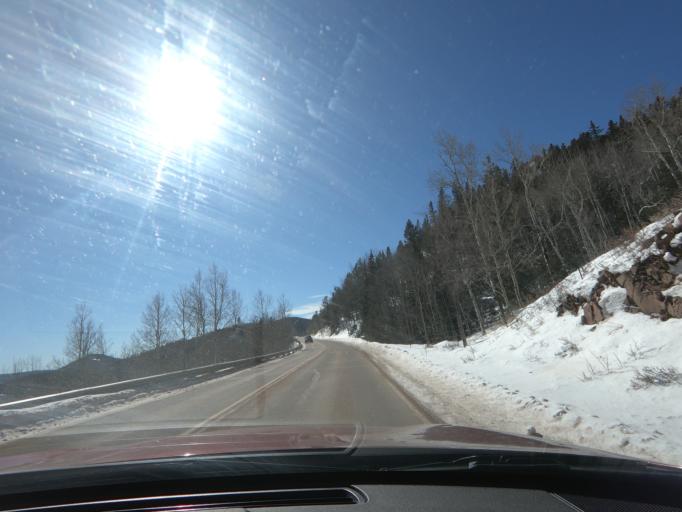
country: US
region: Colorado
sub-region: Teller County
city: Cripple Creek
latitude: 38.7475
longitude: -105.1002
